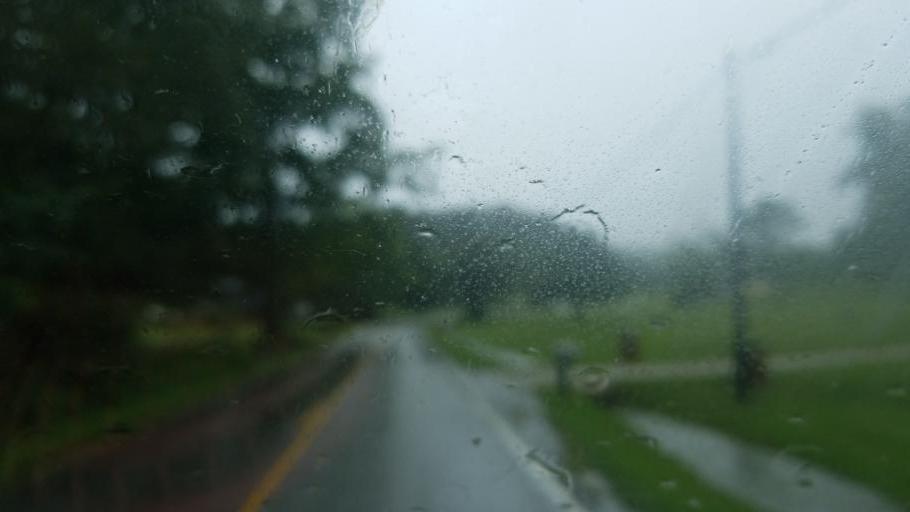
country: US
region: Kentucky
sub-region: Greenup County
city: South Shore
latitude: 38.6692
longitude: -82.9232
